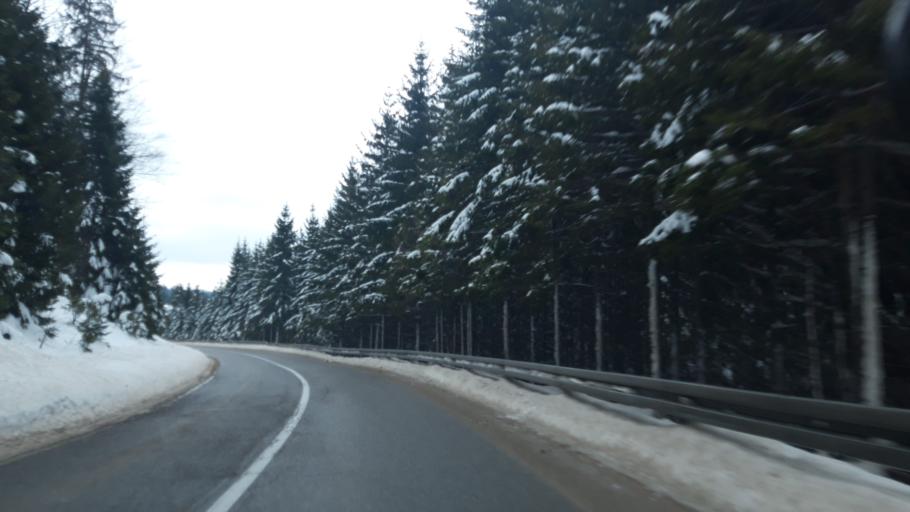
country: BA
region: Republika Srpska
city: Han Pijesak
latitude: 44.1171
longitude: 18.9697
